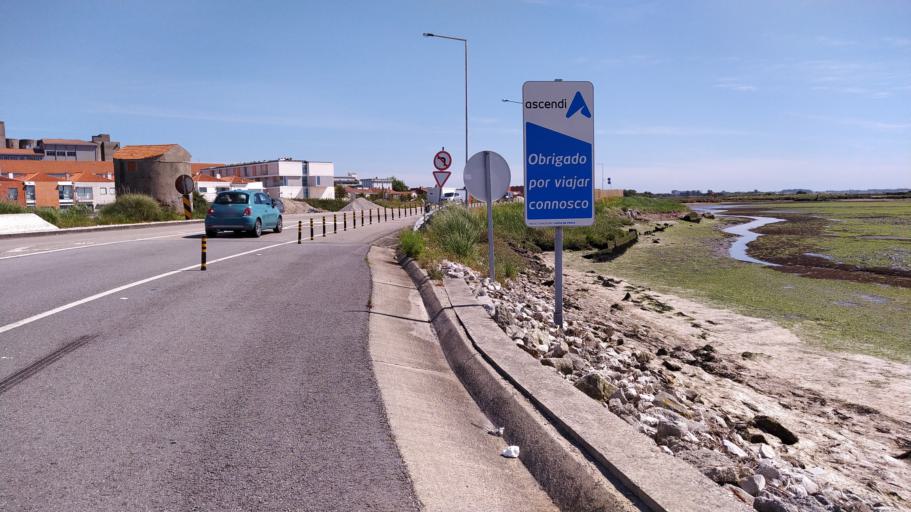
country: PT
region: Aveiro
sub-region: Aveiro
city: Aveiro
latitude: 40.6401
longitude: -8.6594
